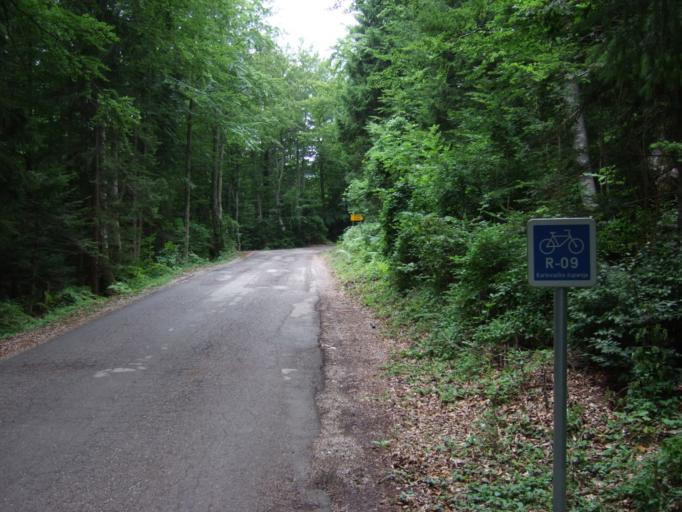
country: HR
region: Licko-Senjska
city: Jezerce
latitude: 44.9256
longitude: 15.5728
